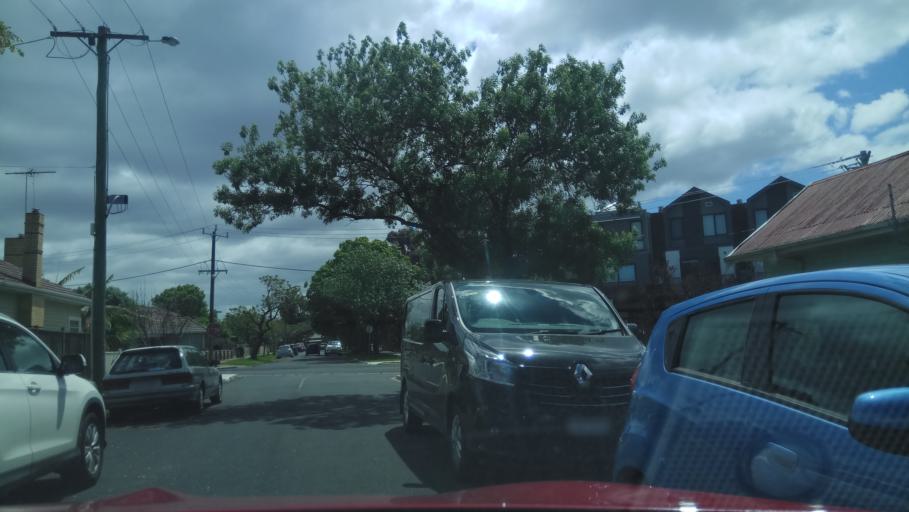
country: AU
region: Victoria
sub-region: Hobsons Bay
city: Newport
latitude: -37.8484
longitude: 144.8887
